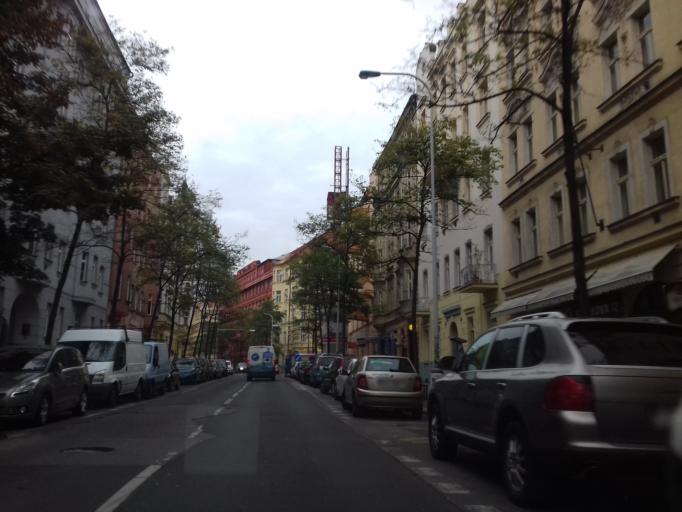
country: CZ
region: Praha
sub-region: Praha 8
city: Karlin
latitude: 50.0792
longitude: 14.4480
